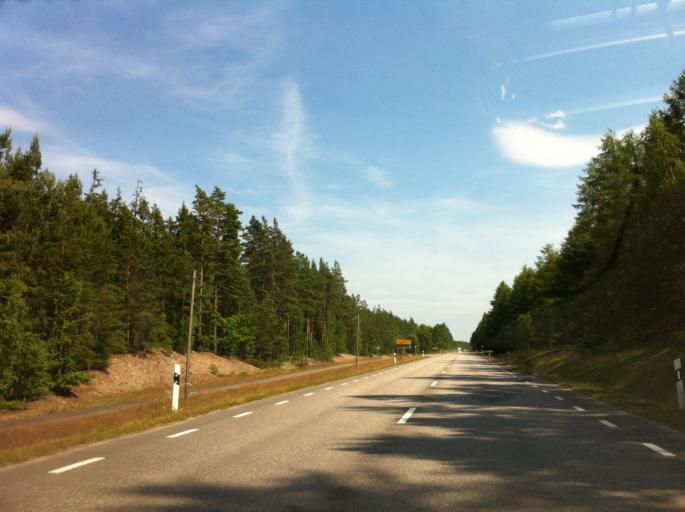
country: SE
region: Kalmar
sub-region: Nybro Kommun
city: Nybro
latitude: 56.8407
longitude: 15.7158
